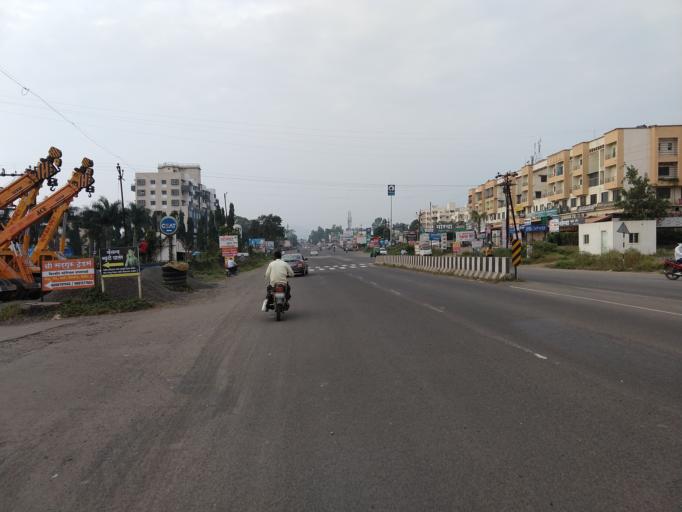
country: IN
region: Maharashtra
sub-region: Pune Division
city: Sasvad
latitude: 18.3549
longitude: 74.0287
